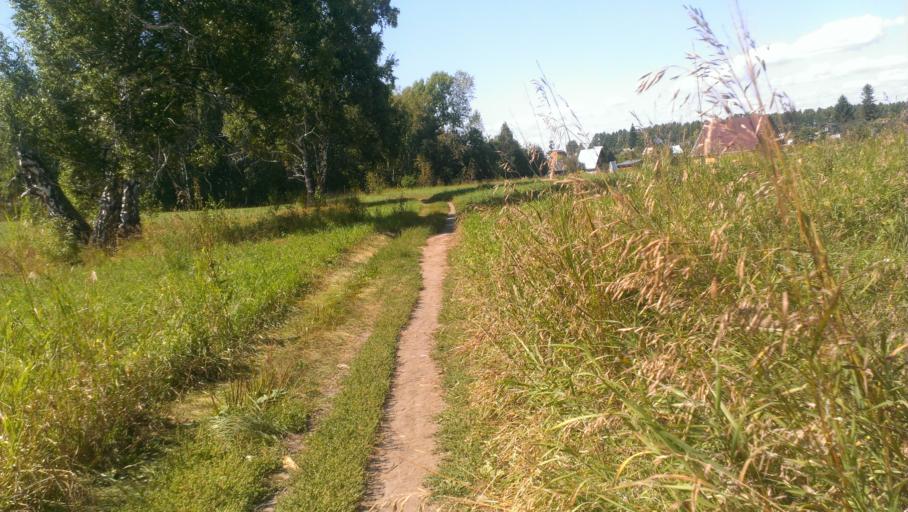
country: RU
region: Altai Krai
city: Nauchnyy Gorodok
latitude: 53.4225
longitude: 83.5139
